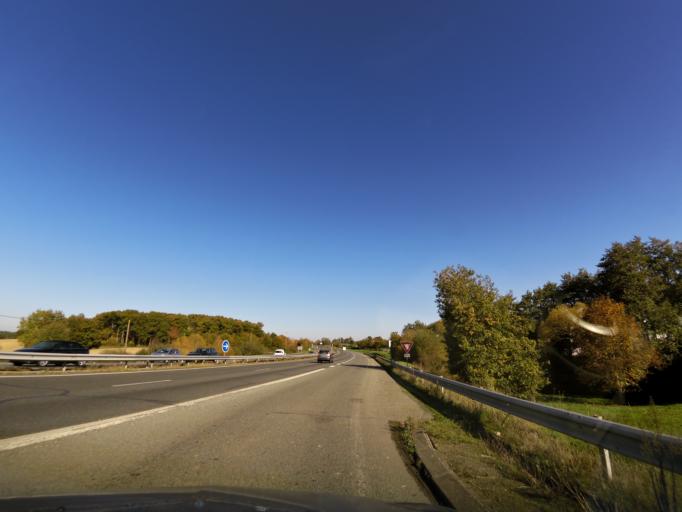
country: FR
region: Brittany
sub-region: Departement d'Ille-et-Vilaine
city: Pance
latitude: 47.8936
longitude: -1.6872
